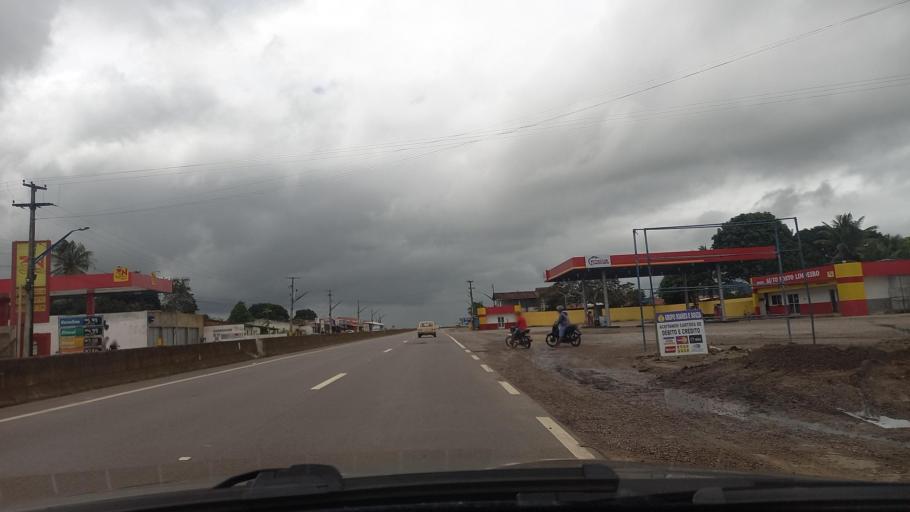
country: BR
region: Alagoas
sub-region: Limoeiro De Anadia
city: Limoeiro de Anadia
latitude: -9.7425
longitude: -36.4713
